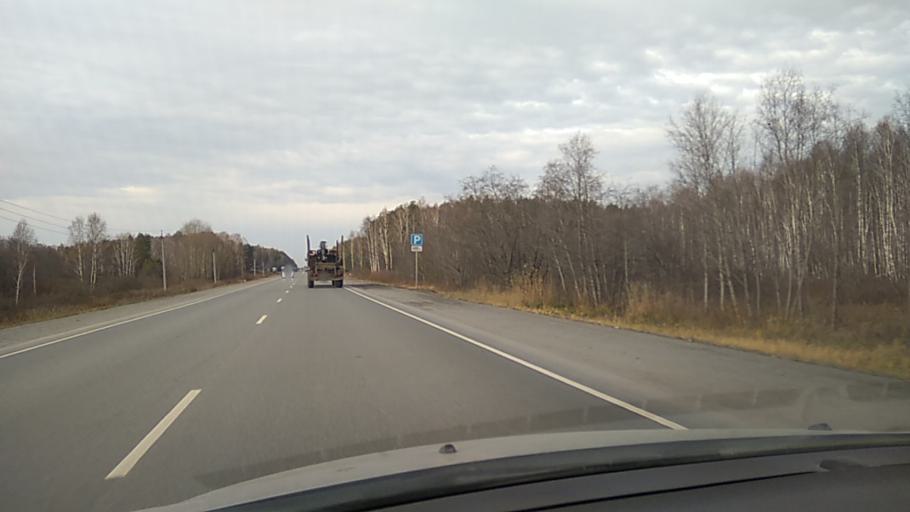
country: RU
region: Sverdlovsk
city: Troitskiy
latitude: 57.0897
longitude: 63.8489
